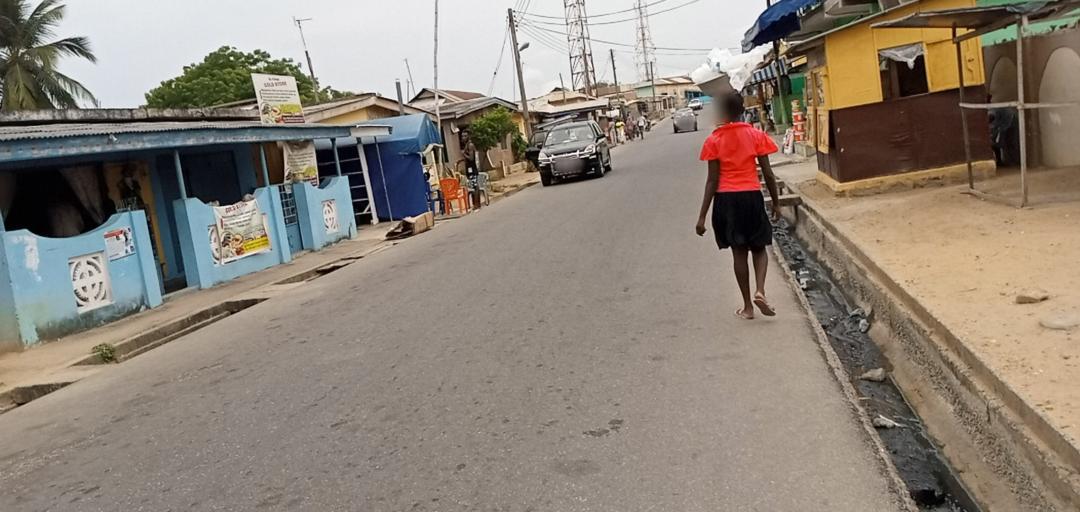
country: GH
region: Central
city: Winneba
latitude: 5.3479
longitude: -0.6265
